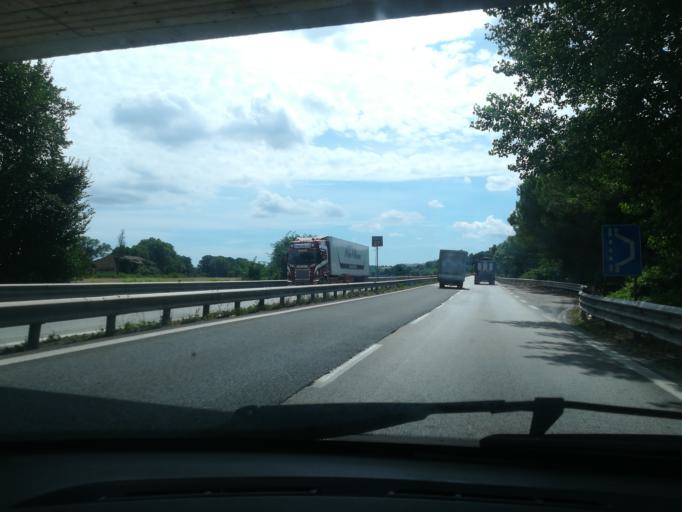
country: IT
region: The Marches
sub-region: Provincia di Macerata
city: Corridonia
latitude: 43.2670
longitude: 13.5242
